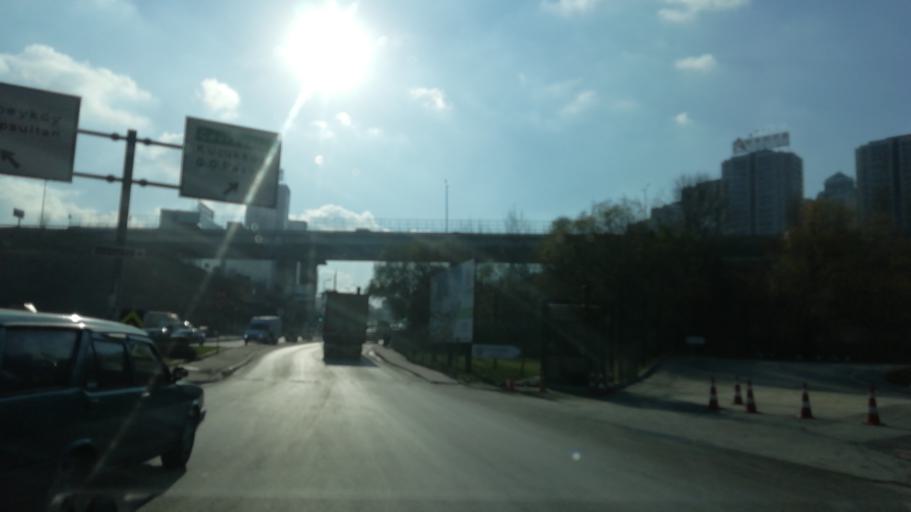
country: TR
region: Istanbul
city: Sultangazi
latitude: 41.0923
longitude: 28.9061
